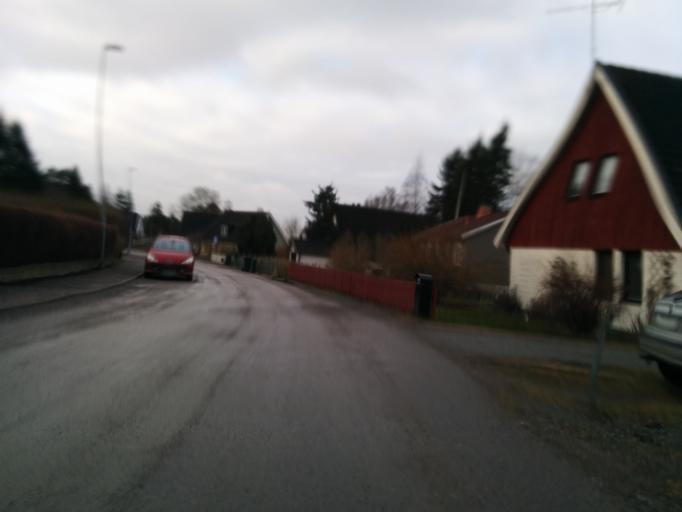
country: SE
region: Stockholm
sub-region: Vallentuna Kommun
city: Vallentuna
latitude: 59.4995
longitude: 18.0742
